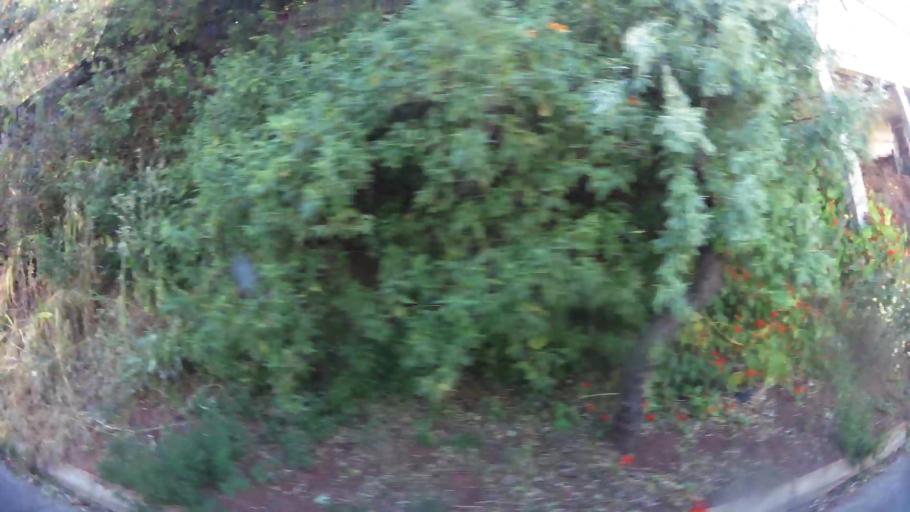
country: CL
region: Valparaiso
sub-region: Provincia de Valparaiso
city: Vina del Mar
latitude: -33.0435
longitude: -71.5661
